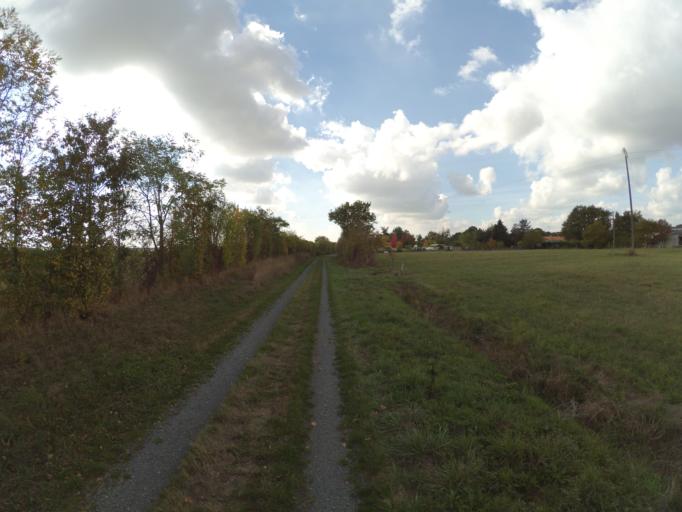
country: FR
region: Pays de la Loire
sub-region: Departement de la Loire-Atlantique
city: Remouille
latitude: 47.0620
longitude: -1.3558
